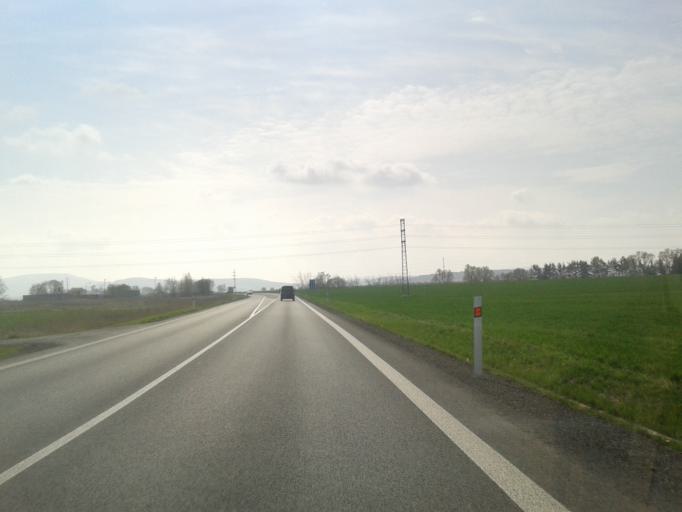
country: CZ
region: Central Bohemia
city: Zebrak
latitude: 49.8626
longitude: 13.8984
